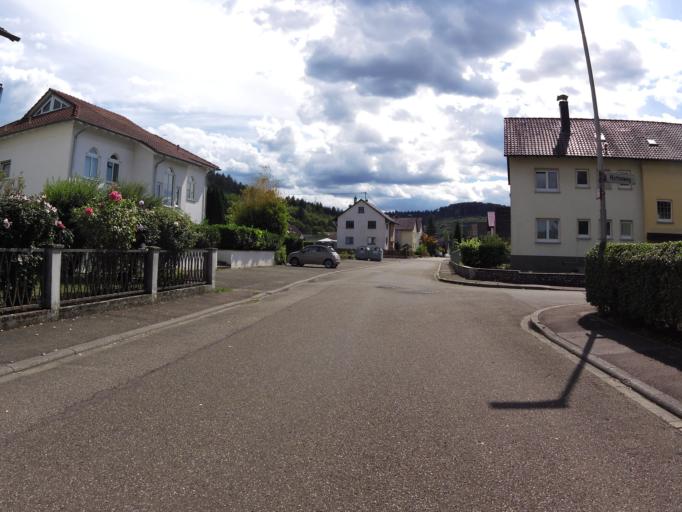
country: DE
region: Baden-Wuerttemberg
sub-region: Freiburg Region
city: Lahr
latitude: 48.3160
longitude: 7.8623
